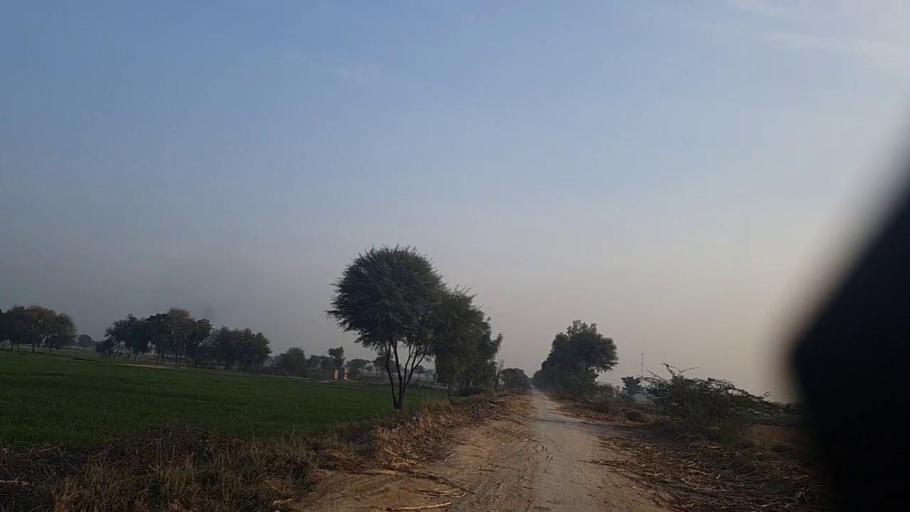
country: PK
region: Sindh
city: Sakrand
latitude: 26.1251
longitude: 68.2301
